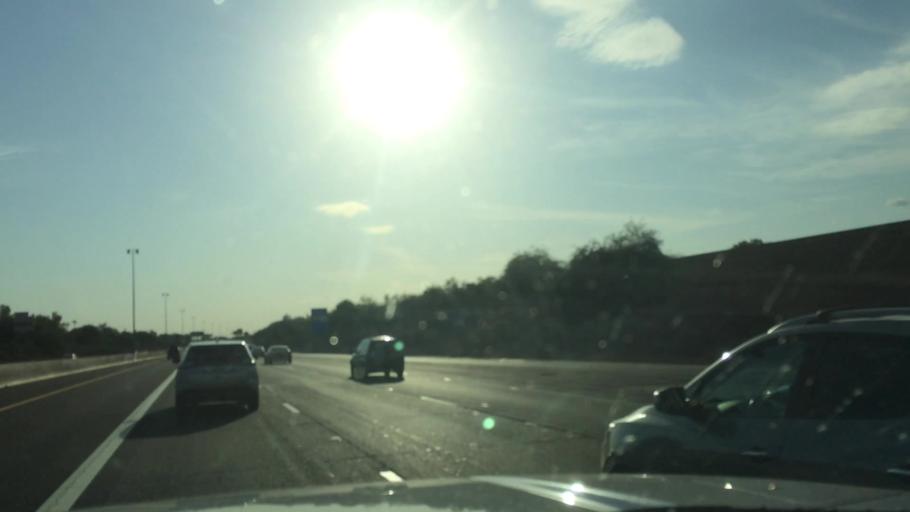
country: US
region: Arizona
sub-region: Maricopa County
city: Peoria
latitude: 33.6681
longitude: -112.2070
